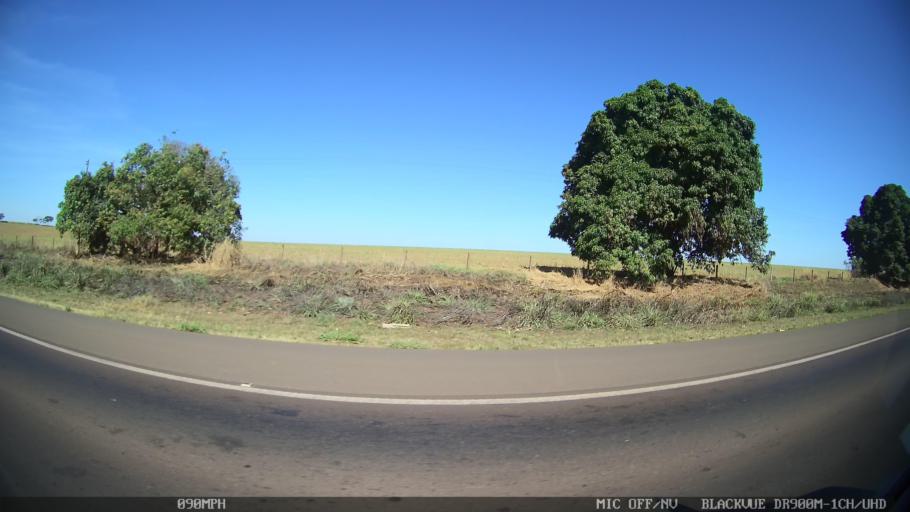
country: BR
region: Sao Paulo
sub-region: Olimpia
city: Olimpia
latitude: -20.6795
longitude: -48.8935
